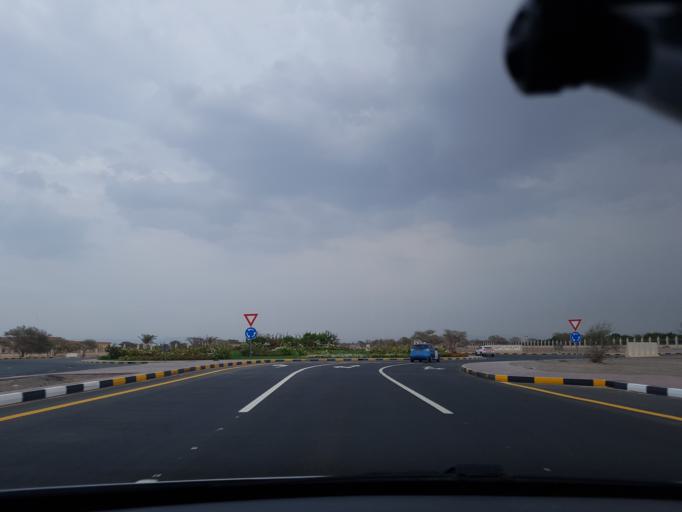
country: AE
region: Ash Shariqah
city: Adh Dhayd
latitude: 25.2675
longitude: 55.9105
